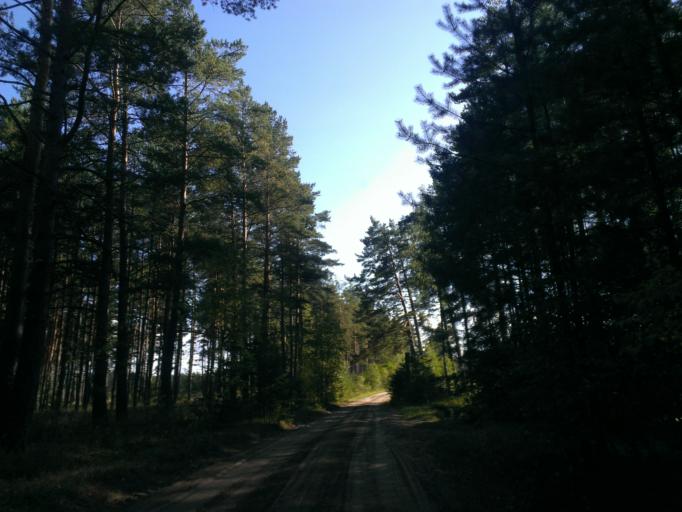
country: LV
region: Adazi
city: Adazi
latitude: 57.0528
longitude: 24.2543
